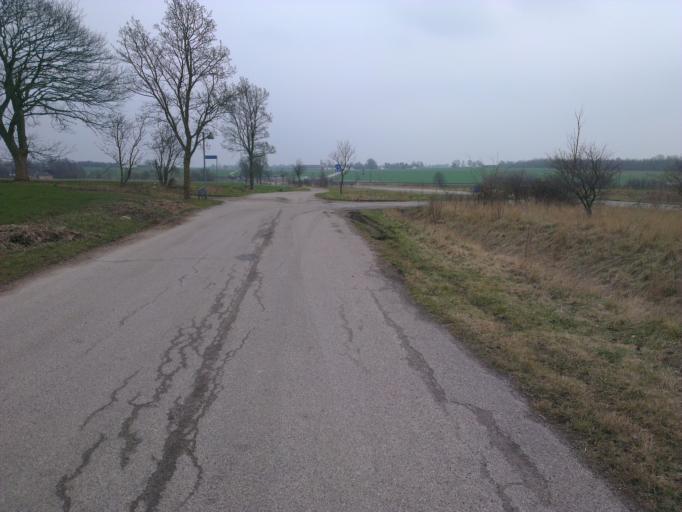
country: DK
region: Capital Region
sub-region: Frederikssund Kommune
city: Frederikssund
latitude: 55.8135
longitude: 12.1055
